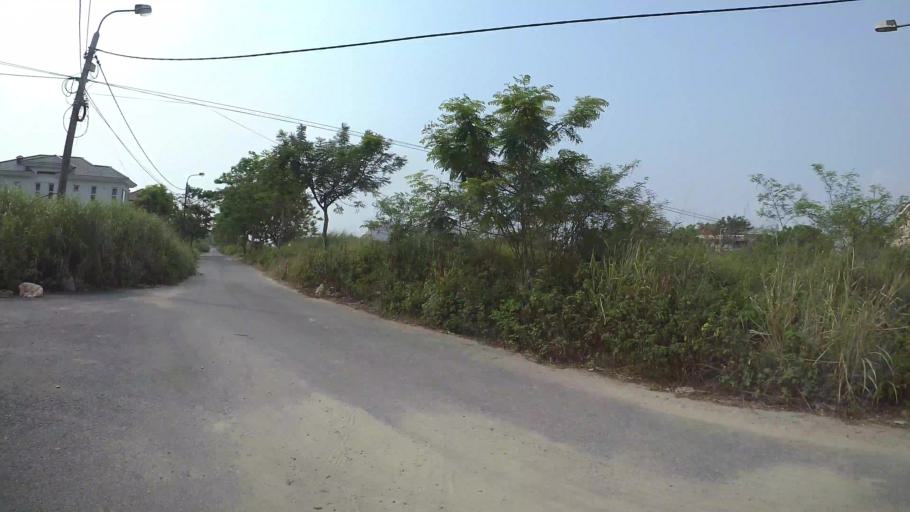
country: VN
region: Da Nang
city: Son Tra
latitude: 16.1058
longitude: 108.2629
